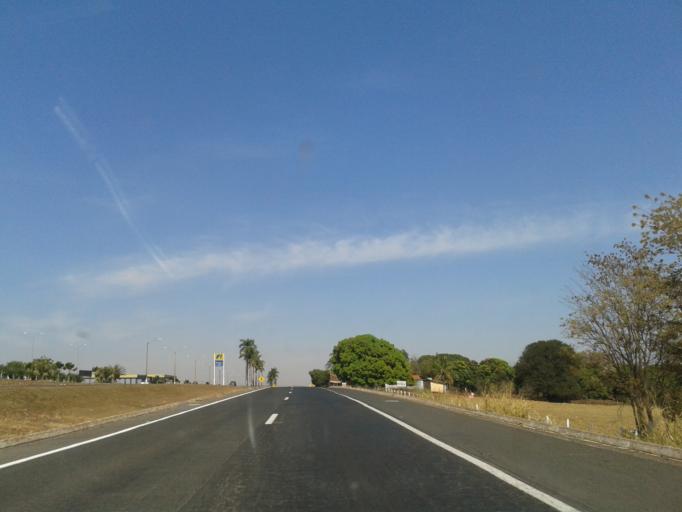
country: BR
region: Goias
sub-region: Goiatuba
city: Goiatuba
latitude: -18.1306
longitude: -49.2854
